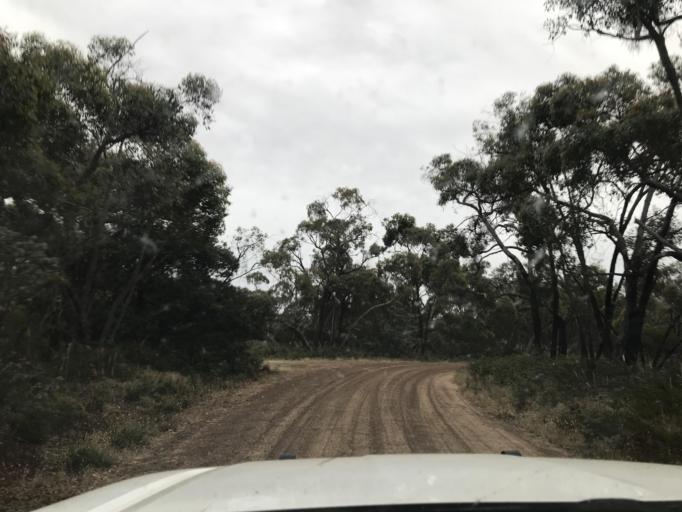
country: AU
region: South Australia
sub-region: Wattle Range
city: Penola
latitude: -37.0931
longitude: 141.5026
